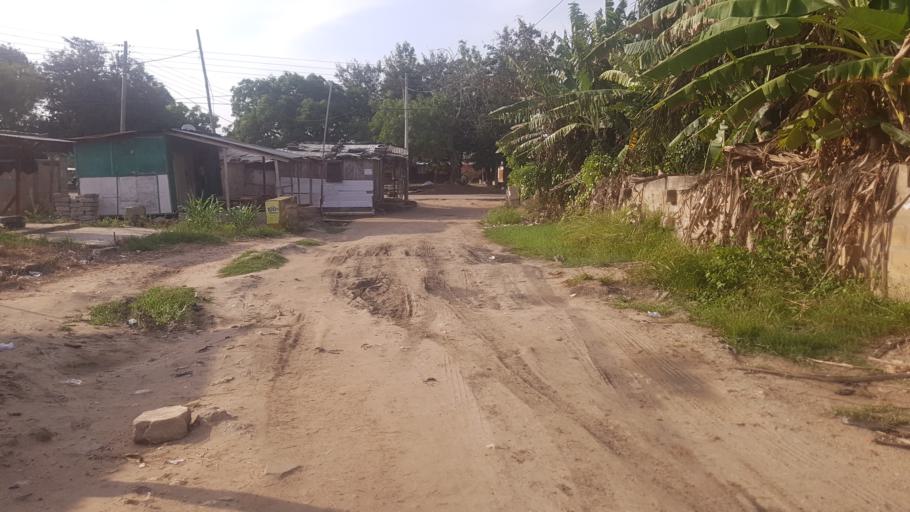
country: GH
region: Central
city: Winneba
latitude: 5.3585
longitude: -0.6311
